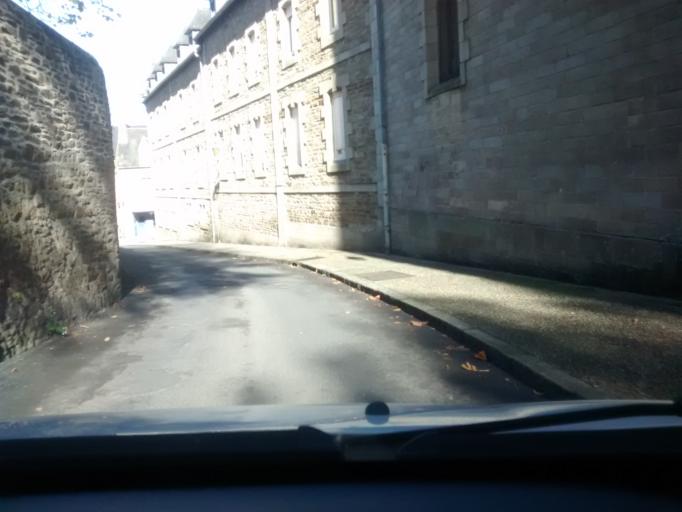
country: FR
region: Brittany
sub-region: Departement des Cotes-d'Armor
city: Treguier
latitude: 48.7867
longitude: -3.2293
